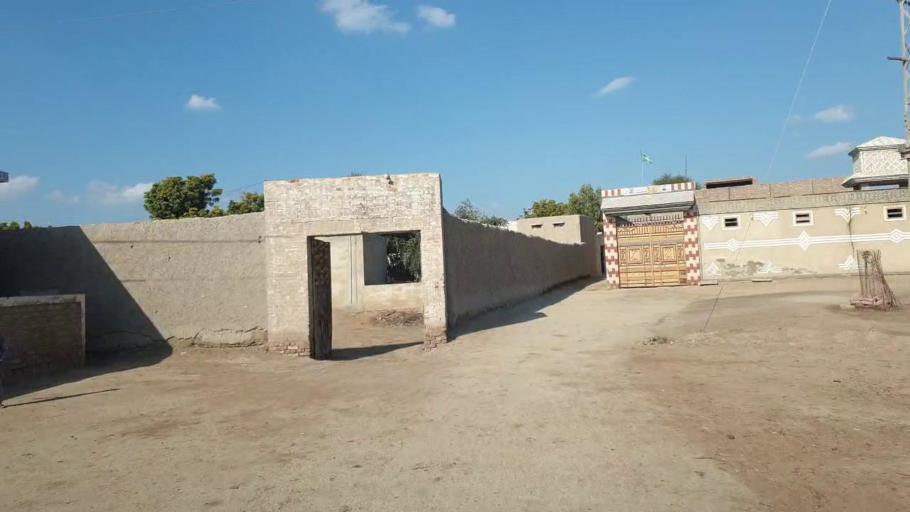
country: PK
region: Sindh
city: Shahpur Chakar
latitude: 26.1027
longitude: 68.5751
